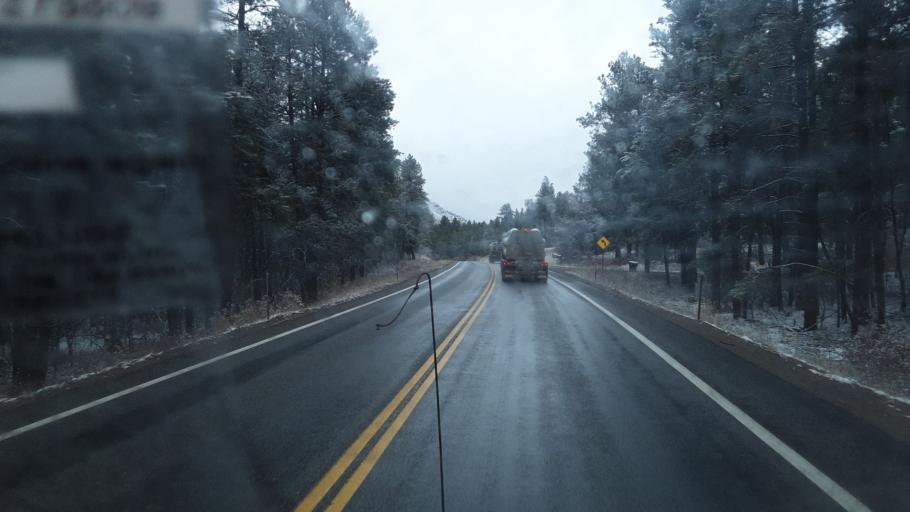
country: US
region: Colorado
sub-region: La Plata County
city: Bayfield
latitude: 37.2186
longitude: -107.3392
